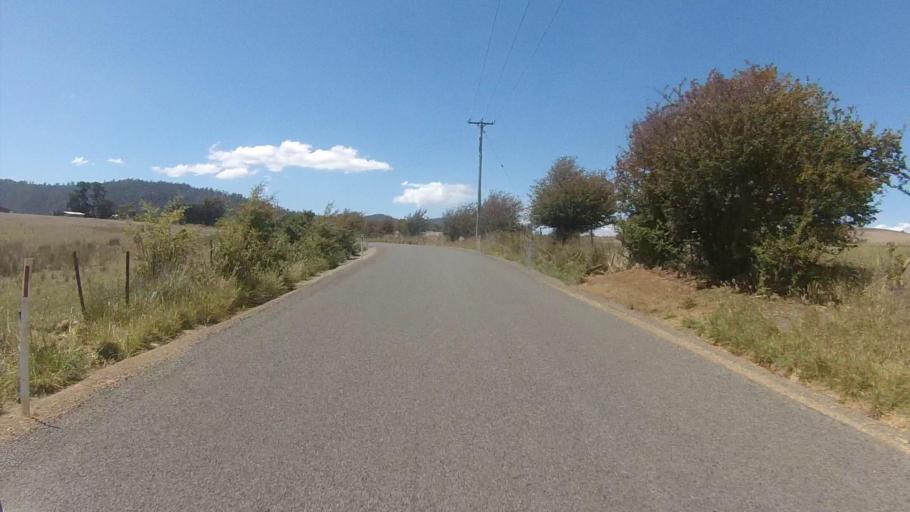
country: AU
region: Tasmania
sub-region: Sorell
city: Sorell
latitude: -42.7627
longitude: 147.6179
